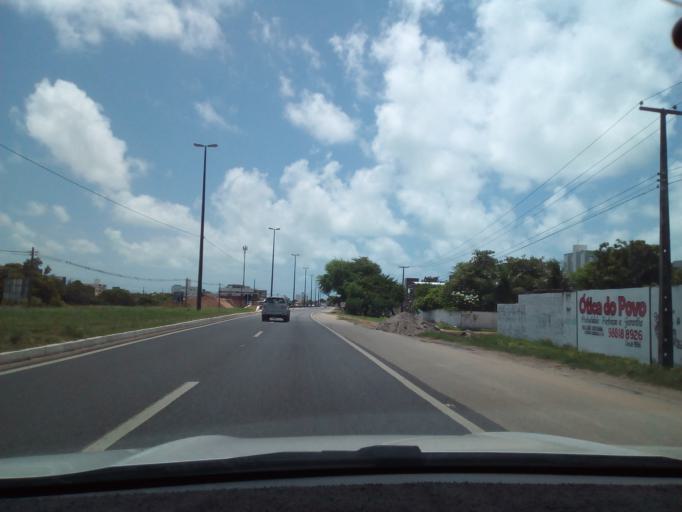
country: BR
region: Paraiba
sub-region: Cabedelo
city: Cabedelo
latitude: -7.0111
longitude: -34.8315
